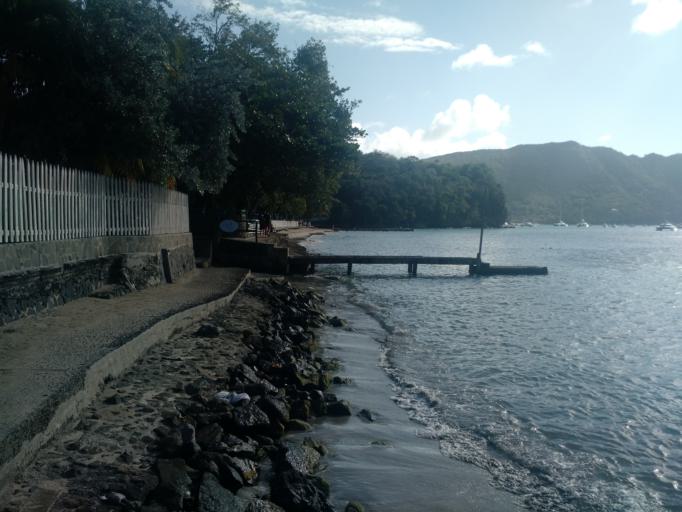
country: VC
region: Grenadines
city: Port Elizabeth
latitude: 13.0065
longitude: -61.2381
